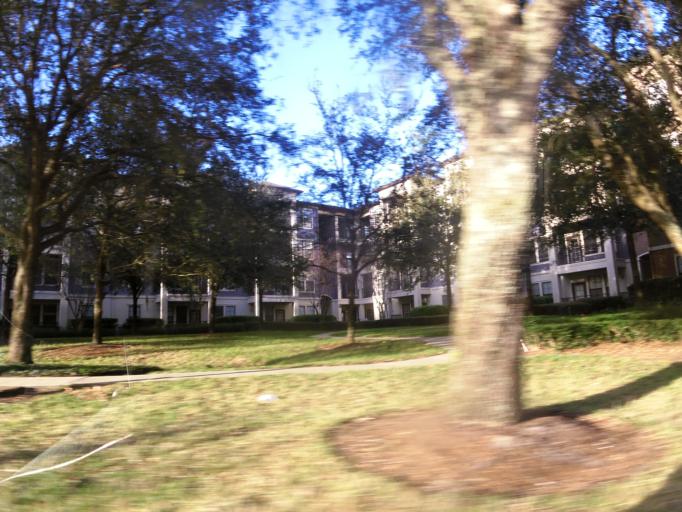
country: US
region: Florida
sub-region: Duval County
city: Jacksonville
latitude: 30.2547
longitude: -81.5523
